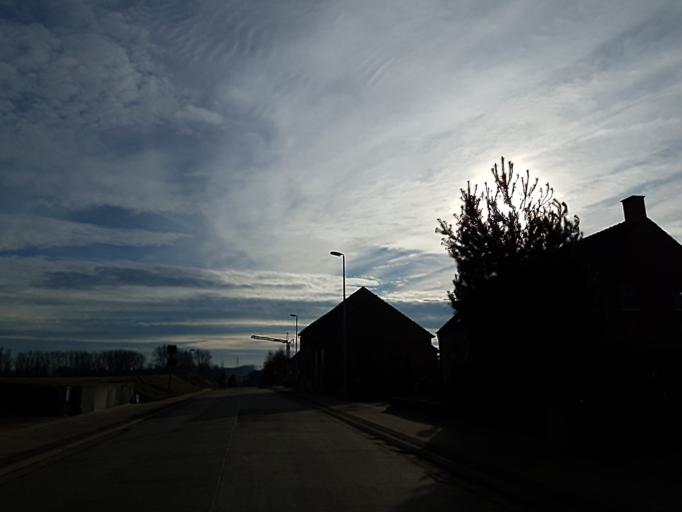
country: BE
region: Flanders
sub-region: Provincie Vlaams-Brabant
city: Boutersem
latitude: 50.8491
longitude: 4.8791
